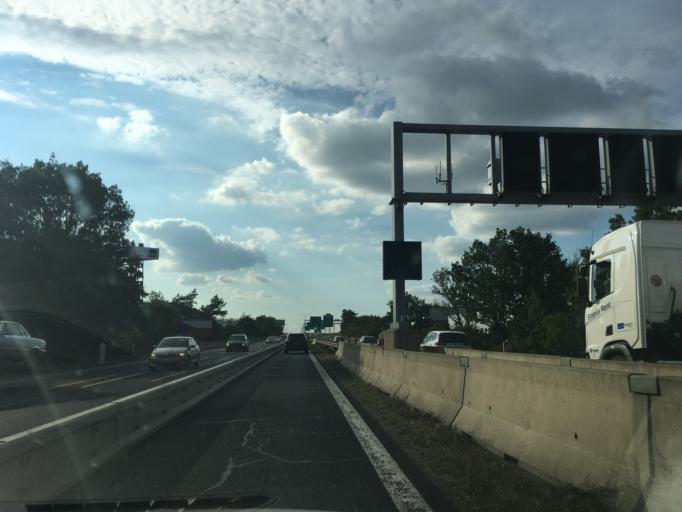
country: CZ
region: Central Bohemia
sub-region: Okres Praha-Vychod
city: Ricany
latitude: 49.9653
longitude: 14.6250
